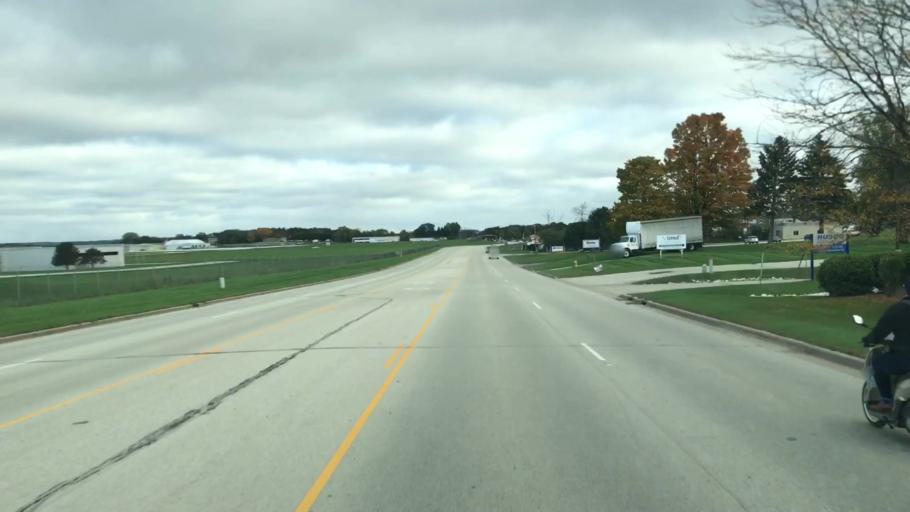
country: US
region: Wisconsin
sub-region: Waukesha County
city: Waukesha
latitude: 43.0346
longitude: -88.2258
